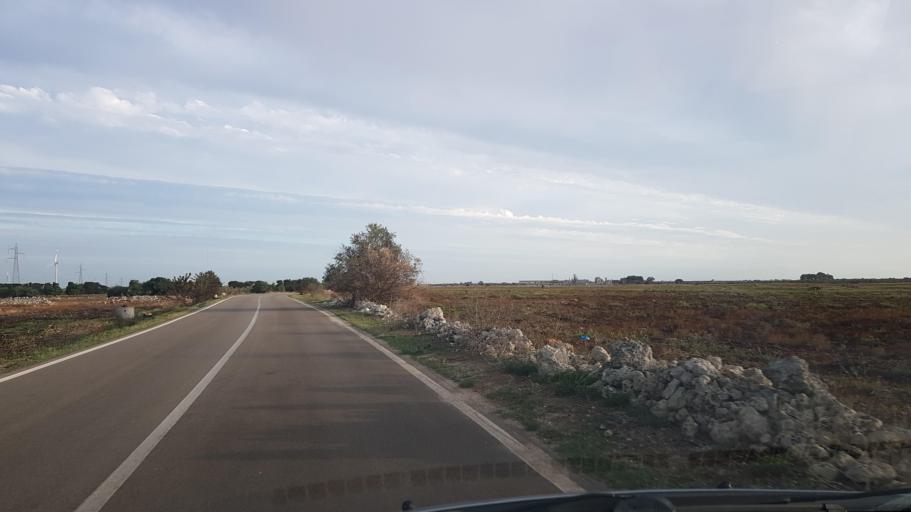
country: IT
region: Apulia
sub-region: Provincia di Lecce
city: Trepuzzi
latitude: 40.4449
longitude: 18.1088
